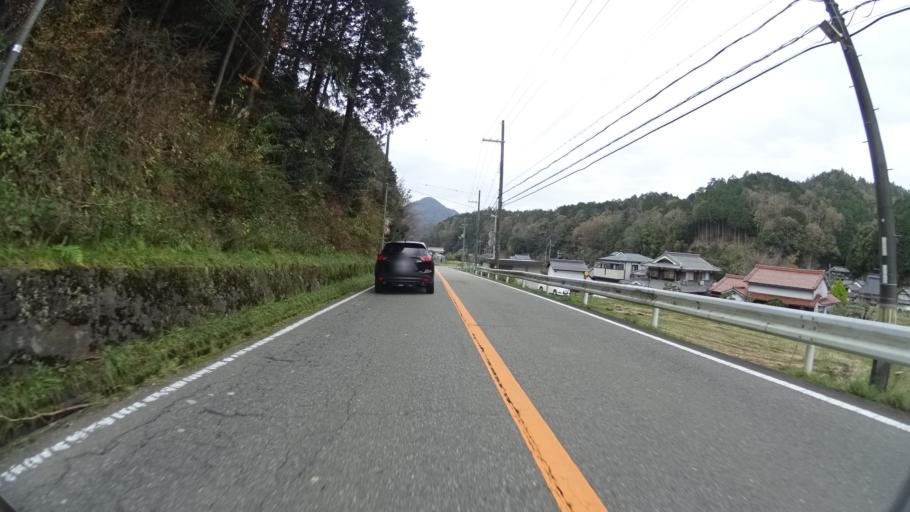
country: JP
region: Hyogo
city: Sasayama
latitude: 35.1361
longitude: 135.2303
